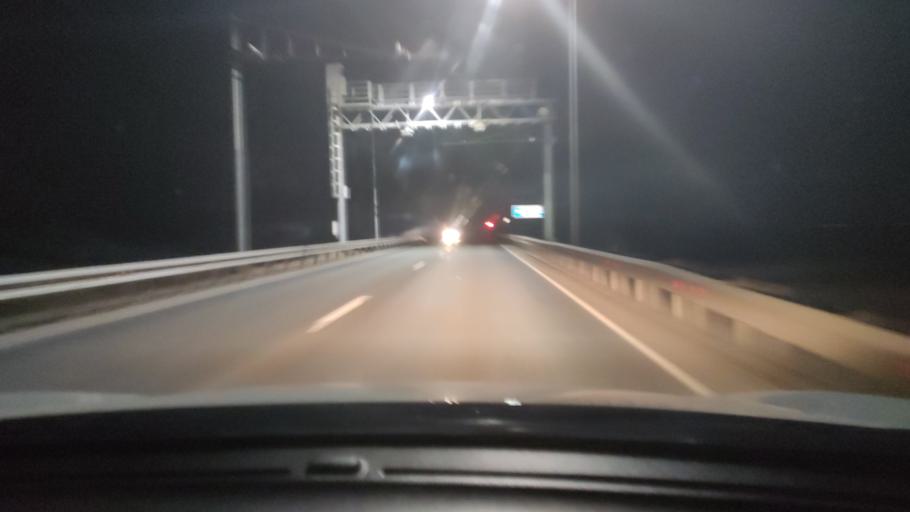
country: RU
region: Tatarstan
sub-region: Alekseyevskiy Rayon
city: Alekseyevskoye
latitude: 55.2614
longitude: 49.9490
